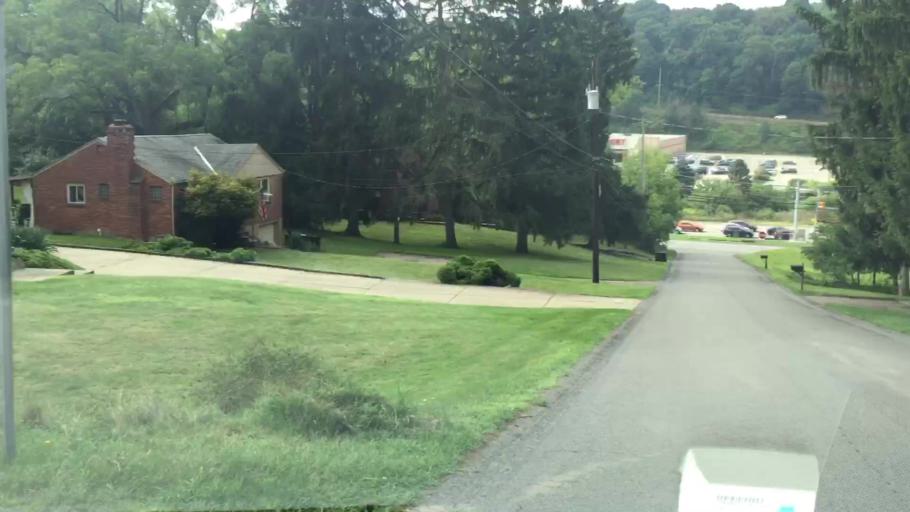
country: US
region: Pennsylvania
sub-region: Allegheny County
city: Franklin Park
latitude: 40.5882
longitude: -80.0409
